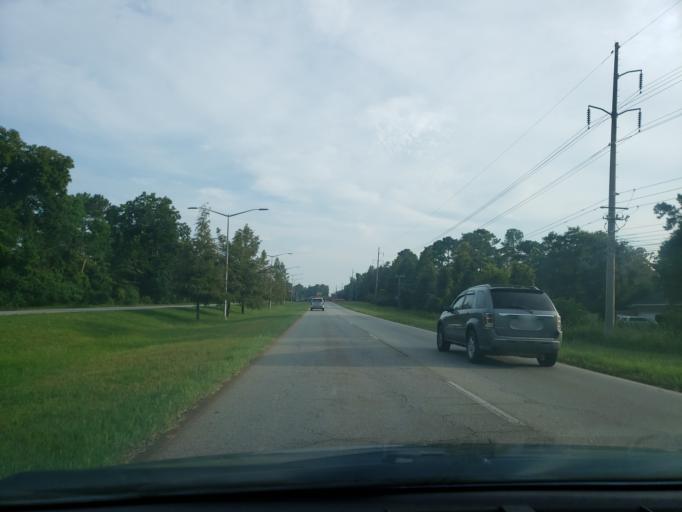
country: US
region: Georgia
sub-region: Dougherty County
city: Albany
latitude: 31.5962
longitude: -84.2194
